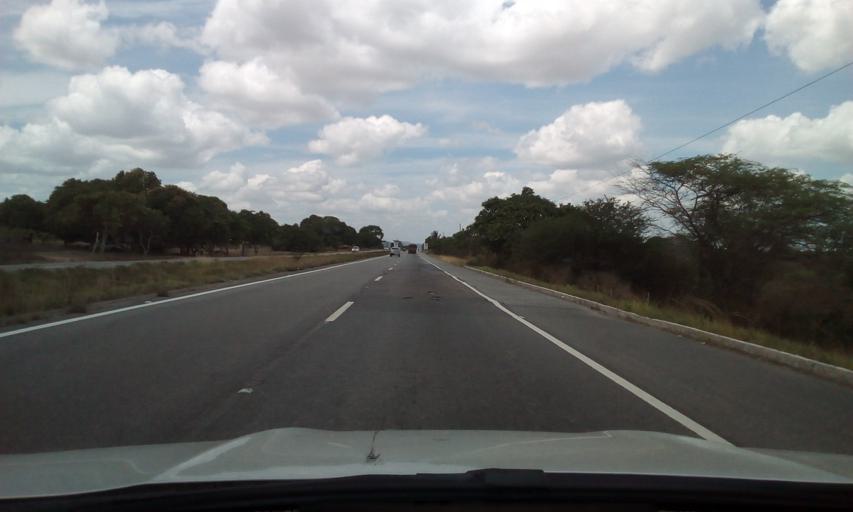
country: BR
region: Paraiba
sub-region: Pilar
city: Pilar
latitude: -7.1861
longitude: -35.2905
